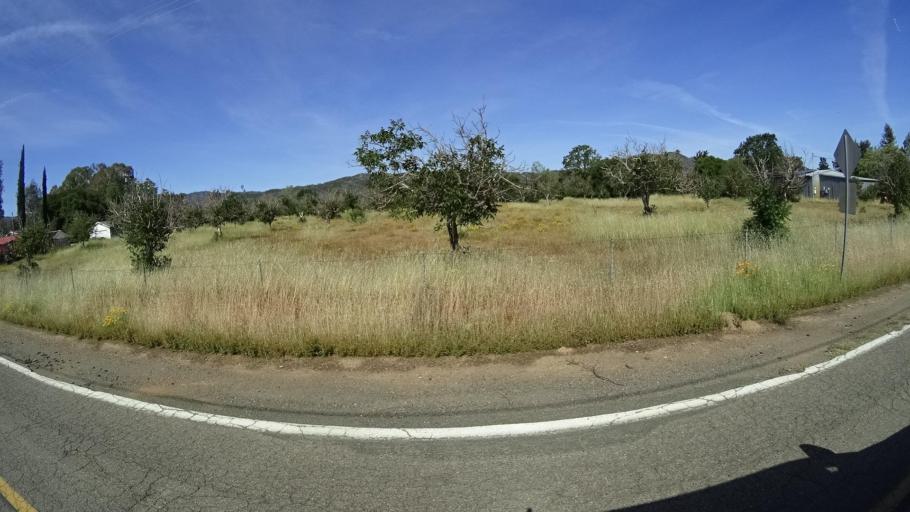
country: US
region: California
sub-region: Lake County
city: Kelseyville
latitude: 38.9584
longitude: -122.8858
